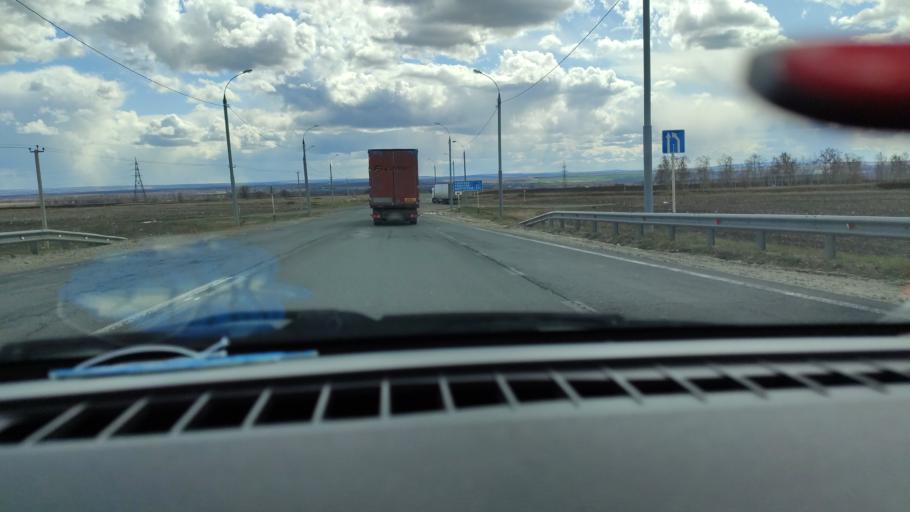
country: RU
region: Samara
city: Varlamovo
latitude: 53.1869
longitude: 48.2911
